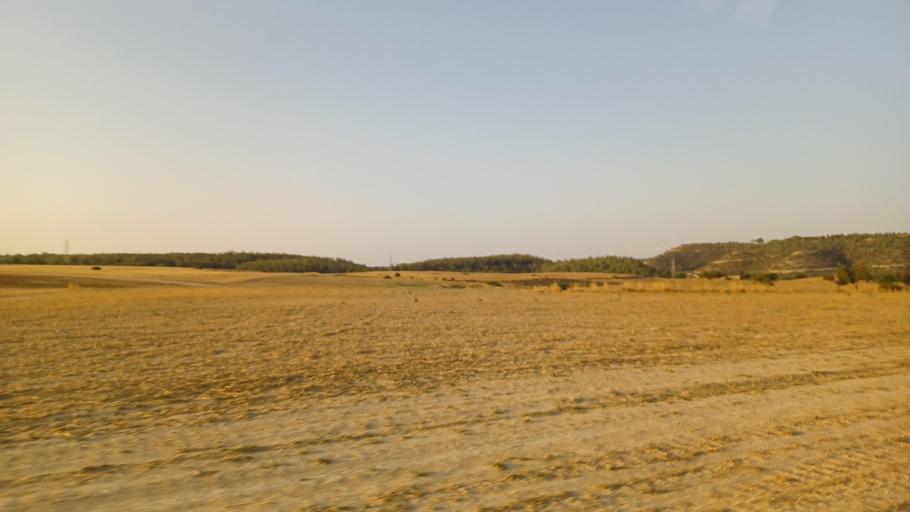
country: CY
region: Lefkosia
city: Lympia
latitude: 34.9960
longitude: 33.5111
